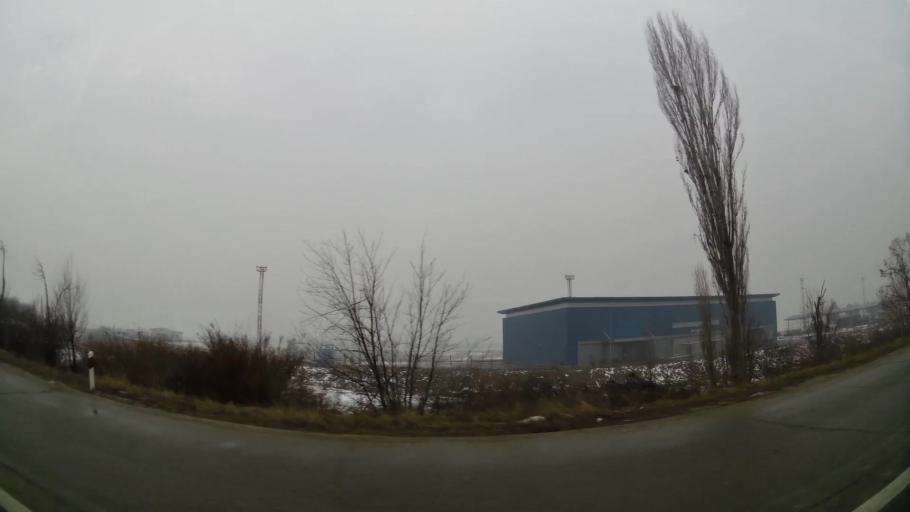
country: MK
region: Petrovec
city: Petrovec
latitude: 41.9528
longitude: 21.6306
